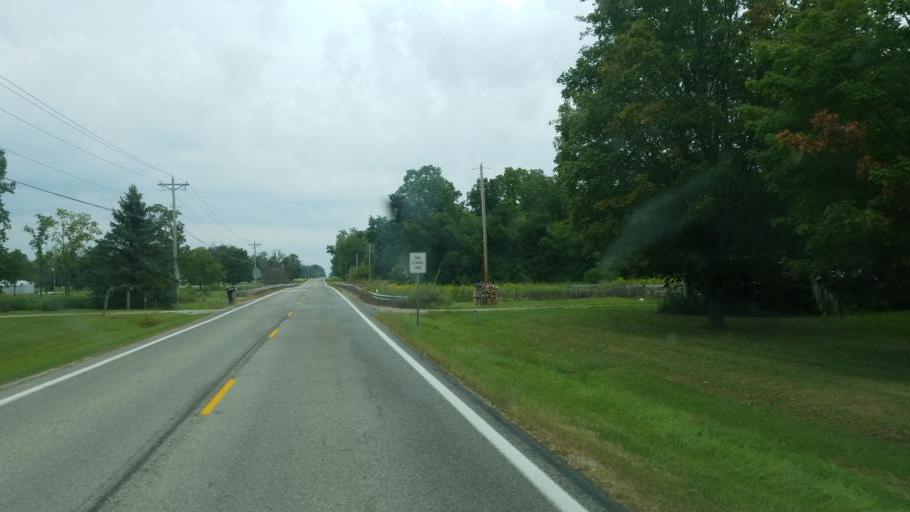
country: US
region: Ohio
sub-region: Crawford County
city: Galion
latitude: 40.6432
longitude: -82.7659
